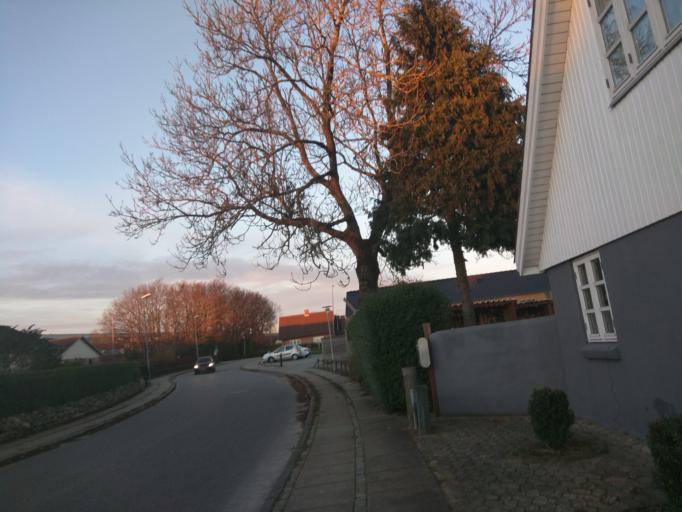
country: DK
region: Central Jutland
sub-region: Skanderborg Kommune
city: Horning
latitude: 56.0871
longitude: 10.0356
